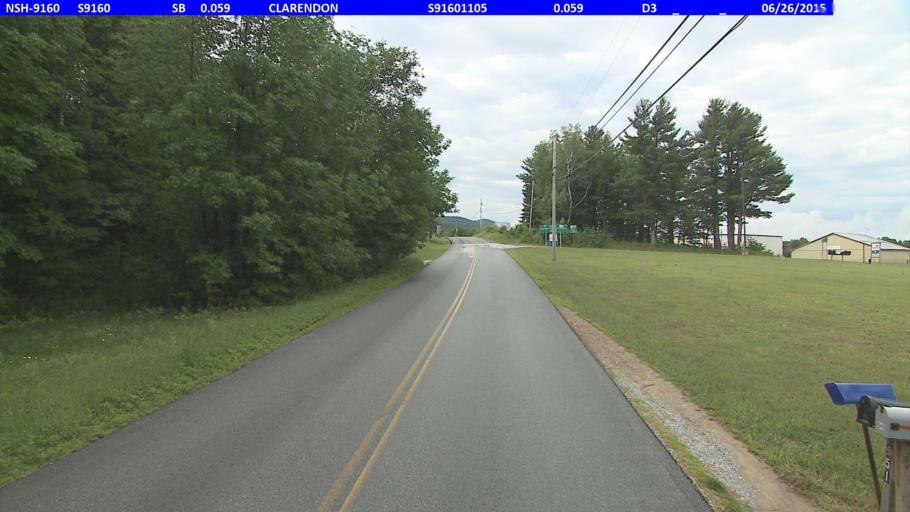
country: US
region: Vermont
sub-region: Rutland County
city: Rutland
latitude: 43.5286
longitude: -72.9444
